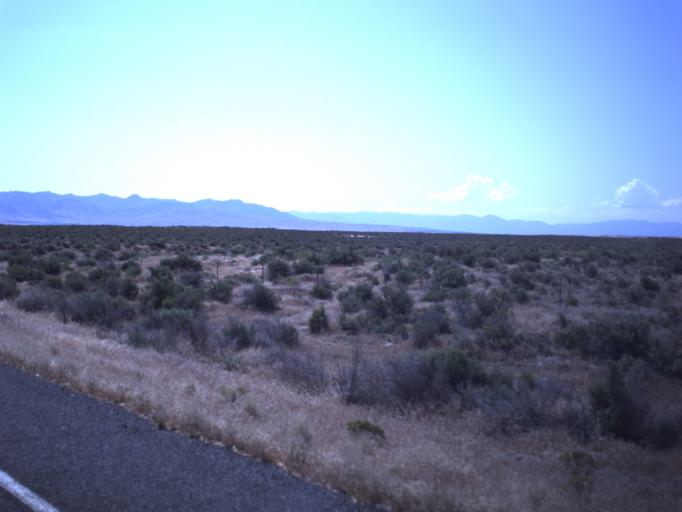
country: US
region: Utah
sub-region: Millard County
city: Delta
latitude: 39.4852
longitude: -112.5327
